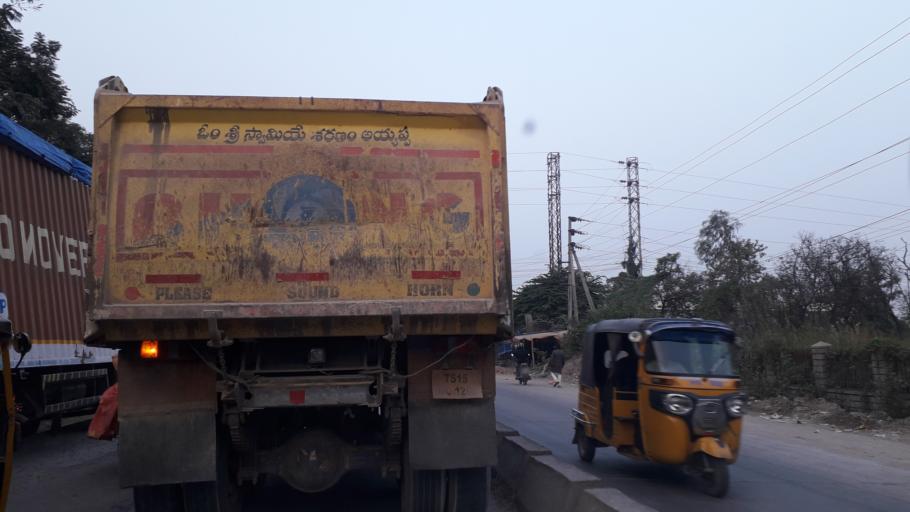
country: IN
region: Telangana
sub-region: Medak
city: Patancheru
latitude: 17.5312
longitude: 78.2546
